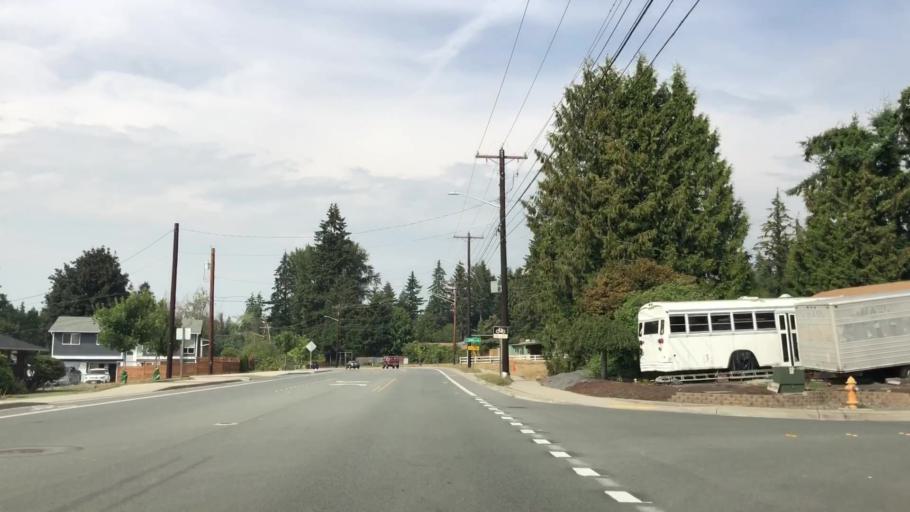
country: US
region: Washington
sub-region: Snohomish County
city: Martha Lake
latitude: 47.8337
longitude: -122.2368
